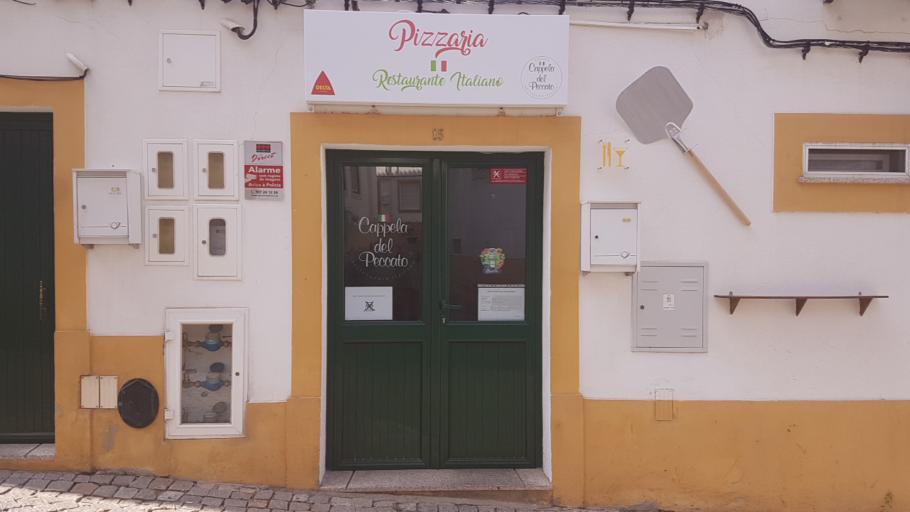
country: PT
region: Portalegre
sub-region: Portalegre
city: Portalegre
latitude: 39.2946
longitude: -7.4304
